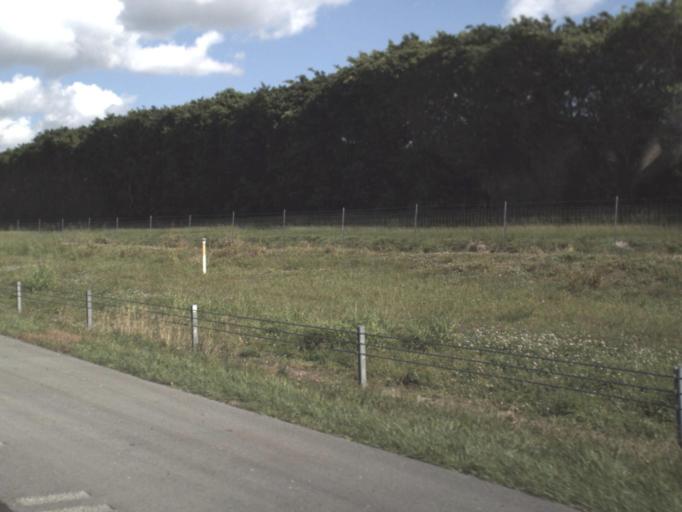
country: US
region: Florida
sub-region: Palm Beach County
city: Kings Point
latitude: 26.4173
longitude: -80.1714
